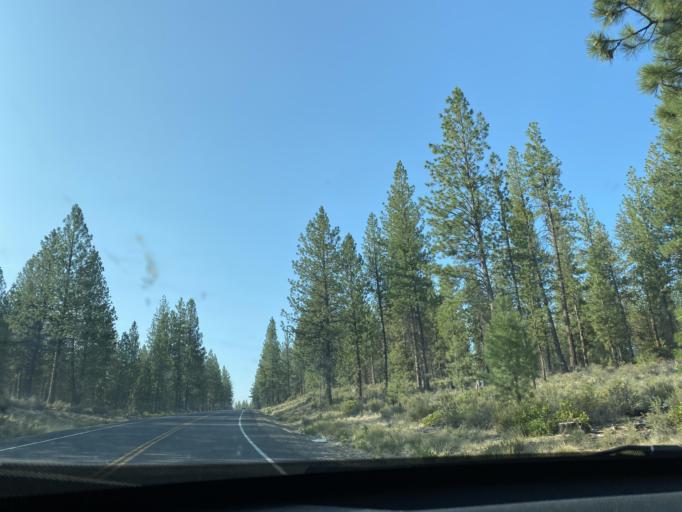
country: US
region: Oregon
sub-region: Deschutes County
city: La Pine
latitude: 43.7242
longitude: -121.4151
